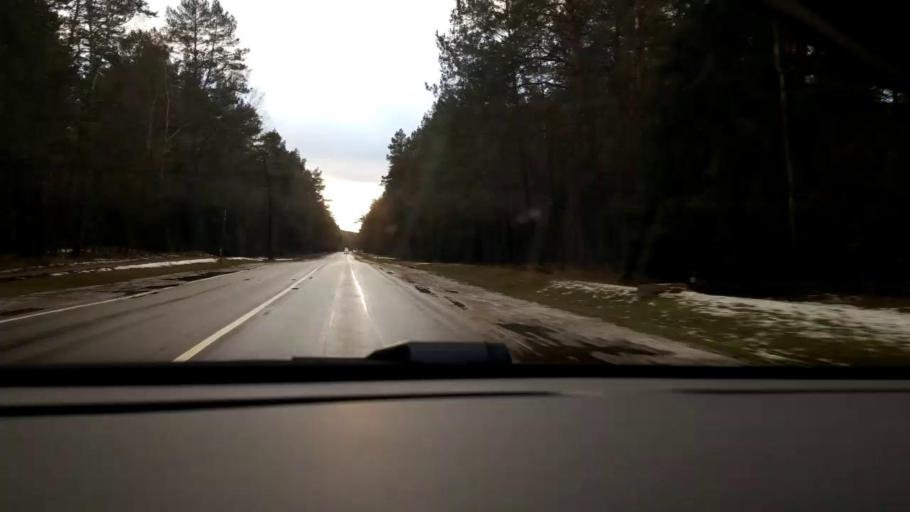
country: LT
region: Vilnius County
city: Rasos
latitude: 54.7685
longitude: 25.3792
